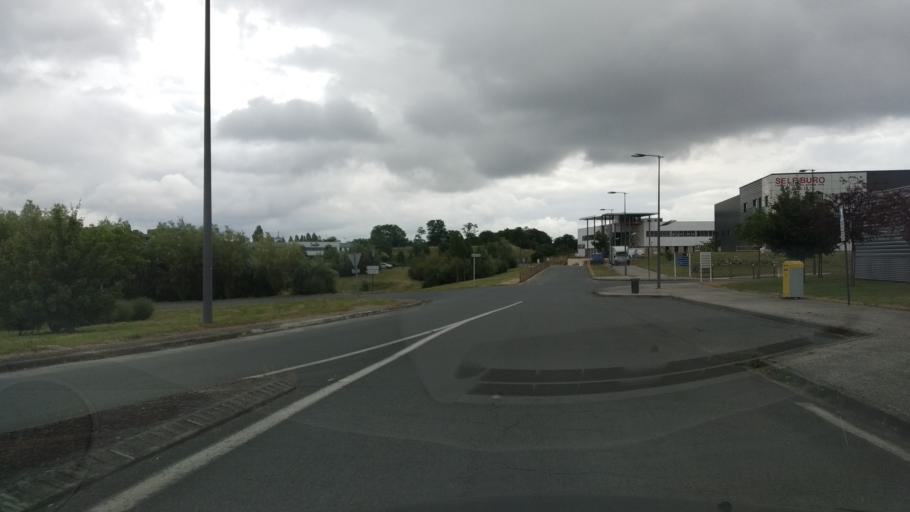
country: FR
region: Poitou-Charentes
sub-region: Departement de la Vienne
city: Biard
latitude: 46.5842
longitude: 0.3150
